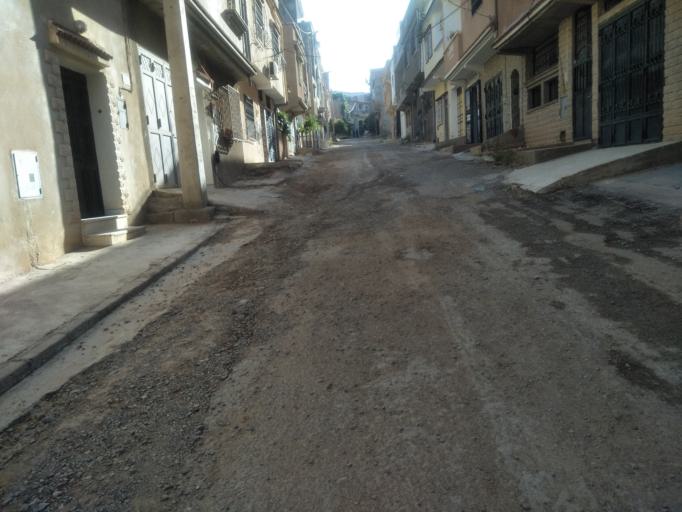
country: DZ
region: Tlemcen
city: Mansoura
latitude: 34.8742
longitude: -1.3701
